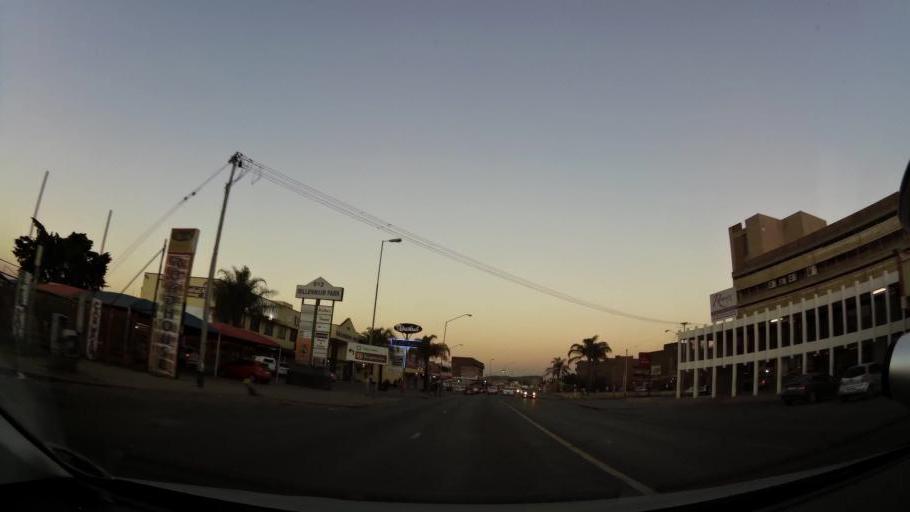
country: ZA
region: Gauteng
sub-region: City of Tshwane Metropolitan Municipality
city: Pretoria
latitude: -25.7192
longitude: 28.1520
